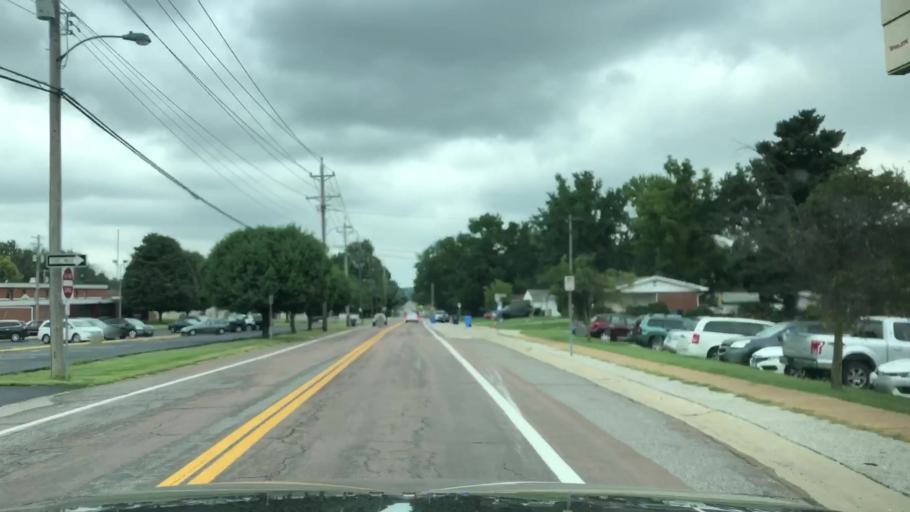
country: US
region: Missouri
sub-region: Saint Louis County
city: Florissant
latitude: 38.8065
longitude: -90.3549
